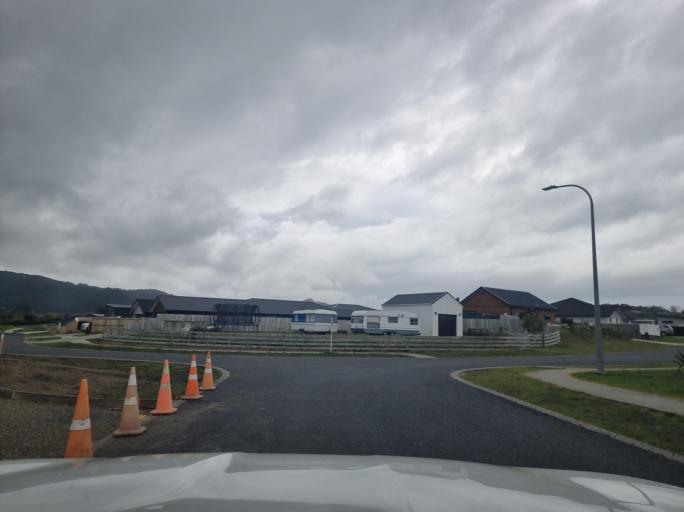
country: NZ
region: Auckland
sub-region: Auckland
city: Wellsford
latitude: -36.0906
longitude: 174.5775
